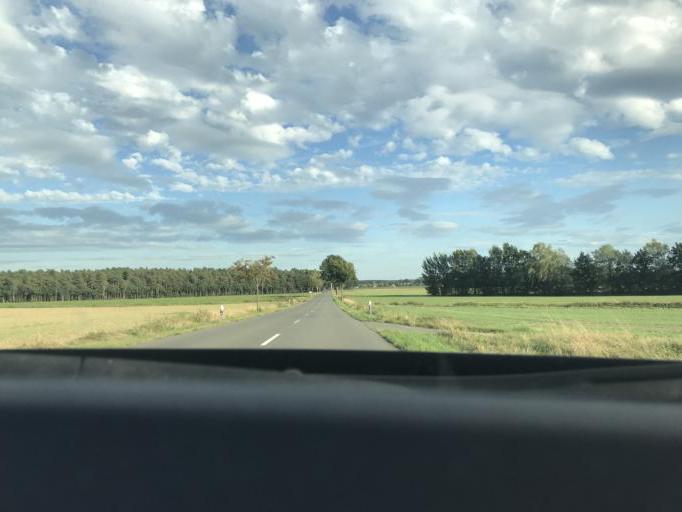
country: DE
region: Lower Saxony
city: Stadensen
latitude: 52.8850
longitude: 10.5317
